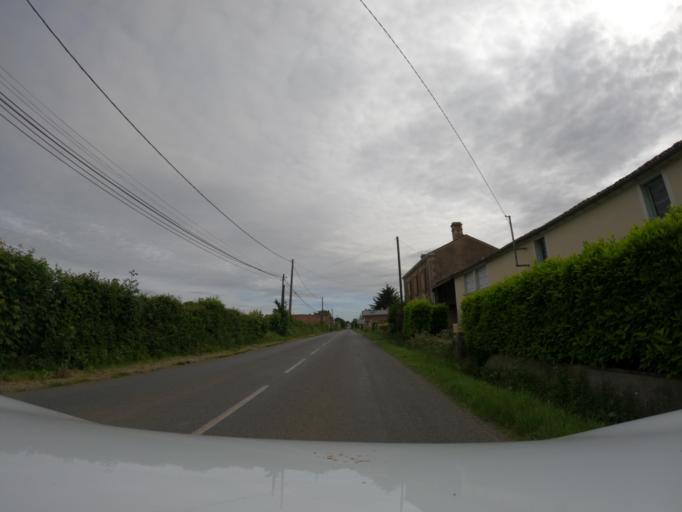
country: FR
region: Pays de la Loire
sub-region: Departement de la Vendee
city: Saint-Hilaire-des-Loges
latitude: 46.4803
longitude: -0.6615
